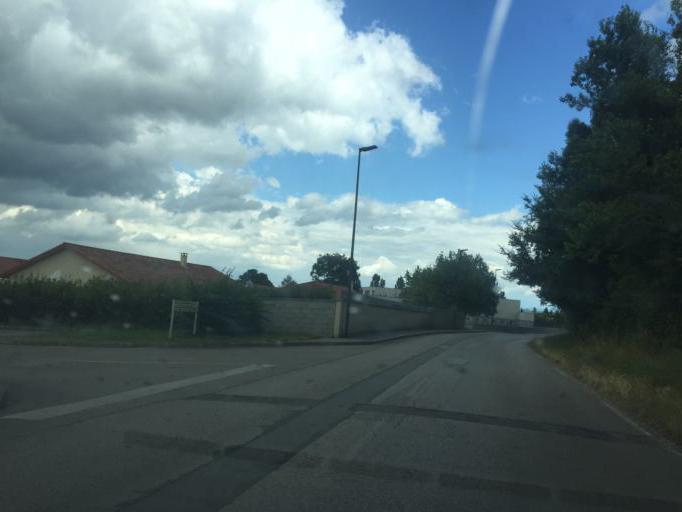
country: FR
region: Rhone-Alpes
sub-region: Departement de l'Isere
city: Pont-de-Cheruy
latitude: 45.7667
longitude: 5.1907
